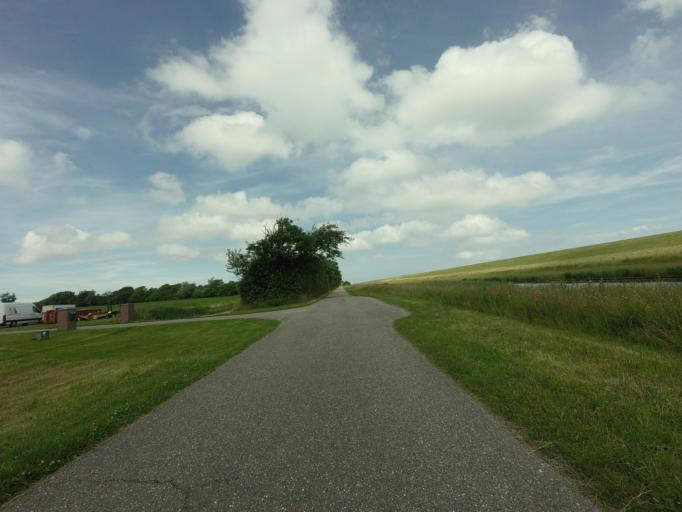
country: NL
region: North Holland
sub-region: Gemeente Texel
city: Den Burg
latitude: 53.1116
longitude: 4.8973
